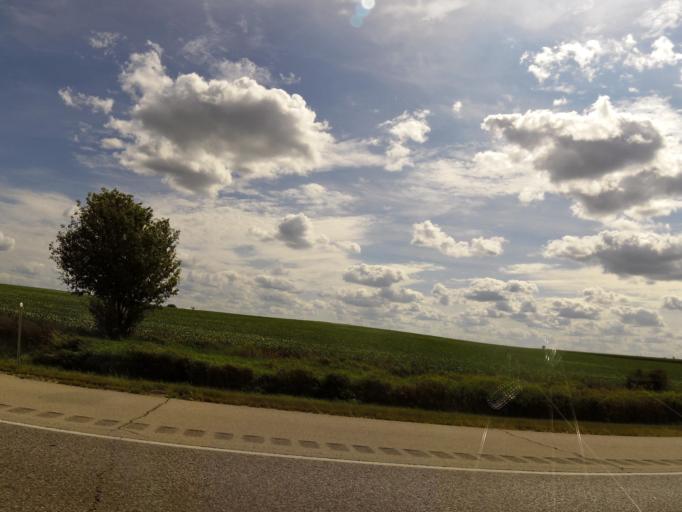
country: US
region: Illinois
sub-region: Ogle County
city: Rochelle
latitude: 41.9051
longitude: -89.0064
